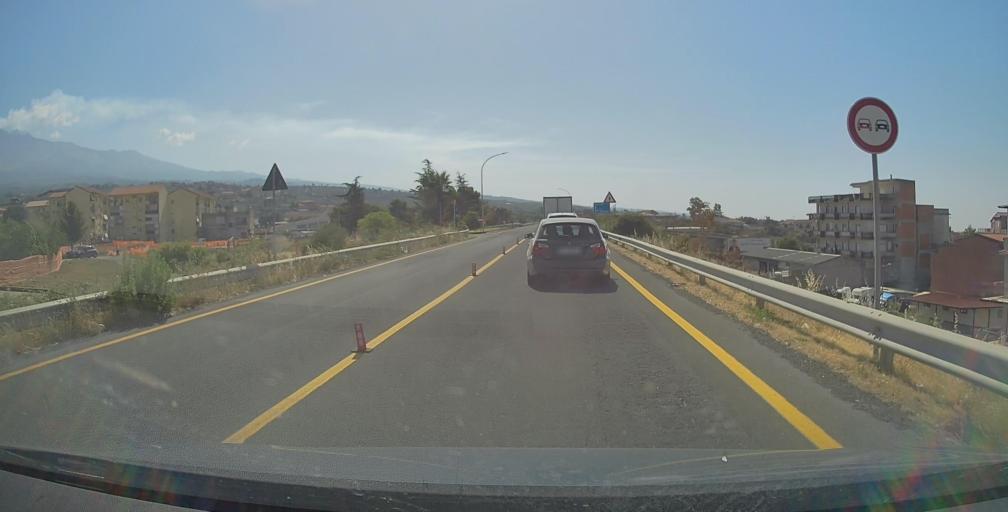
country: IT
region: Sicily
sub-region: Catania
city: Adrano
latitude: 37.6750
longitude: 14.8398
